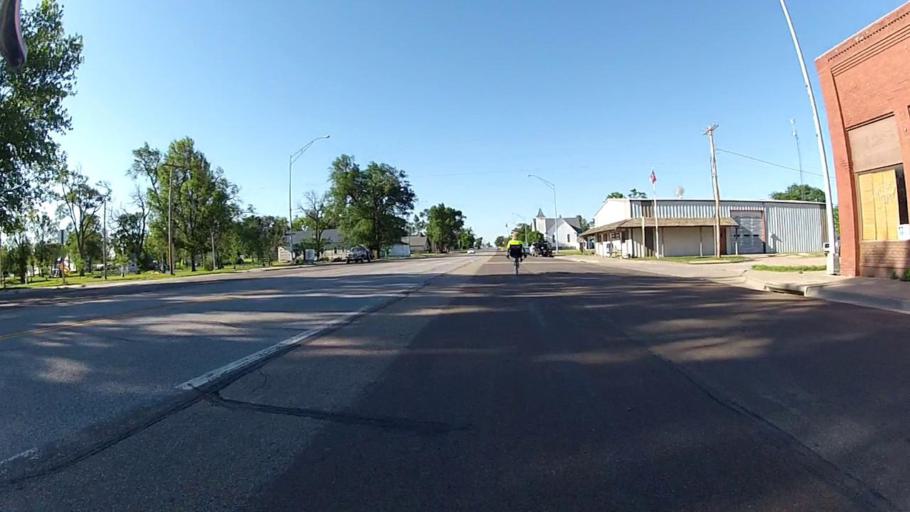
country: US
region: Kansas
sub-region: Ford County
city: Dodge City
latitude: 37.6387
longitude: -99.7539
